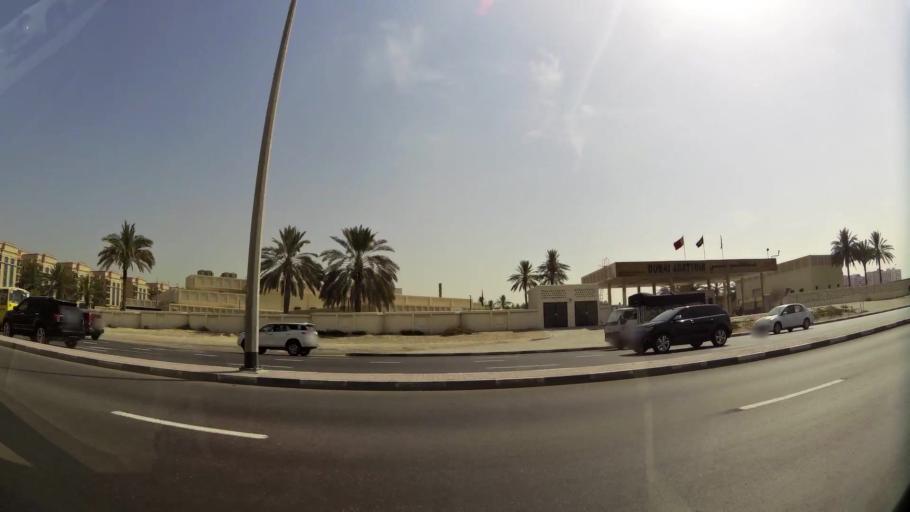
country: AE
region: Ash Shariqah
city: Sharjah
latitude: 25.2840
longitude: 55.3911
